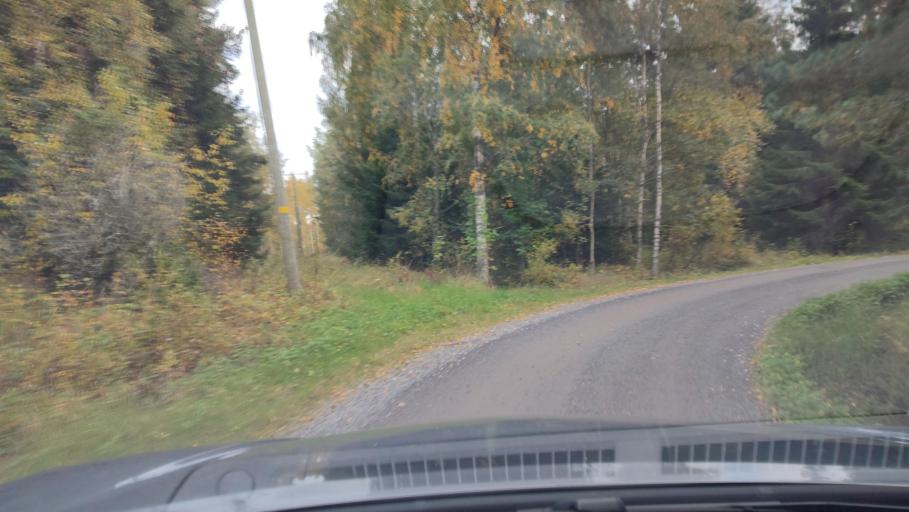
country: FI
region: Ostrobothnia
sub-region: Sydosterbotten
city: Kristinestad
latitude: 62.2317
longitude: 21.4044
